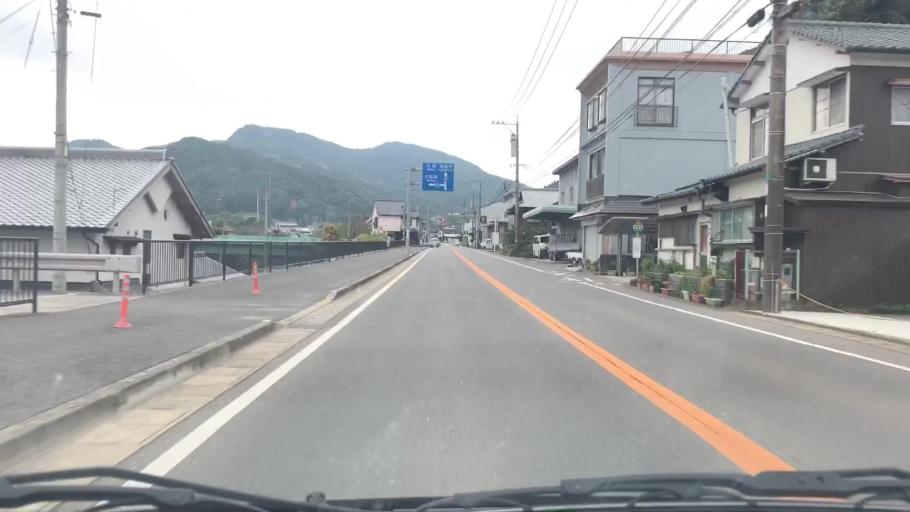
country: JP
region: Saga Prefecture
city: Ureshinomachi-shimojuku
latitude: 33.0931
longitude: 129.9767
